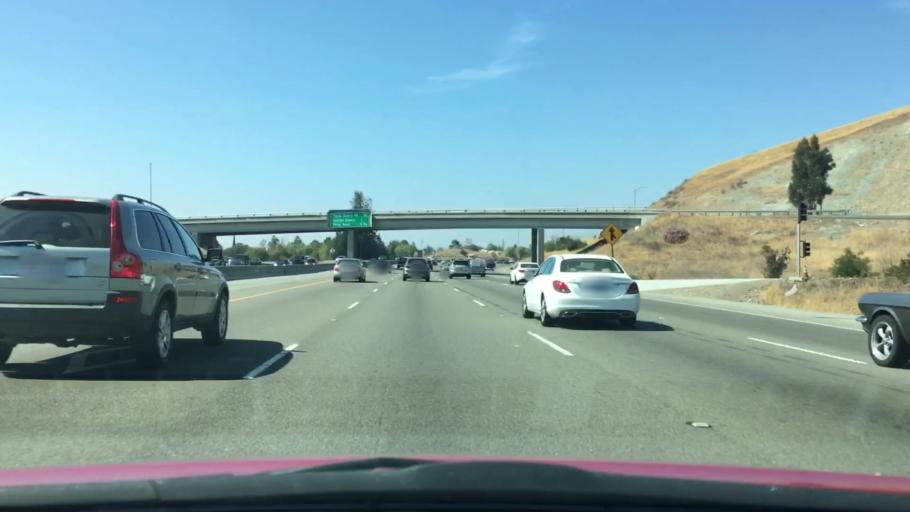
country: US
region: California
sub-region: Santa Clara County
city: Seven Trees
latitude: 37.2807
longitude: -121.8076
